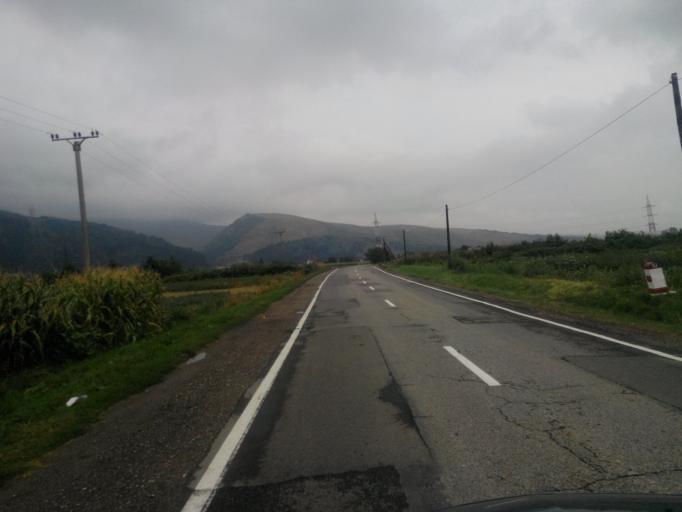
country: RO
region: Cluj
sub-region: Comuna Moldovenesti
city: Moldovenesti
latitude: 46.5141
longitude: 23.6795
